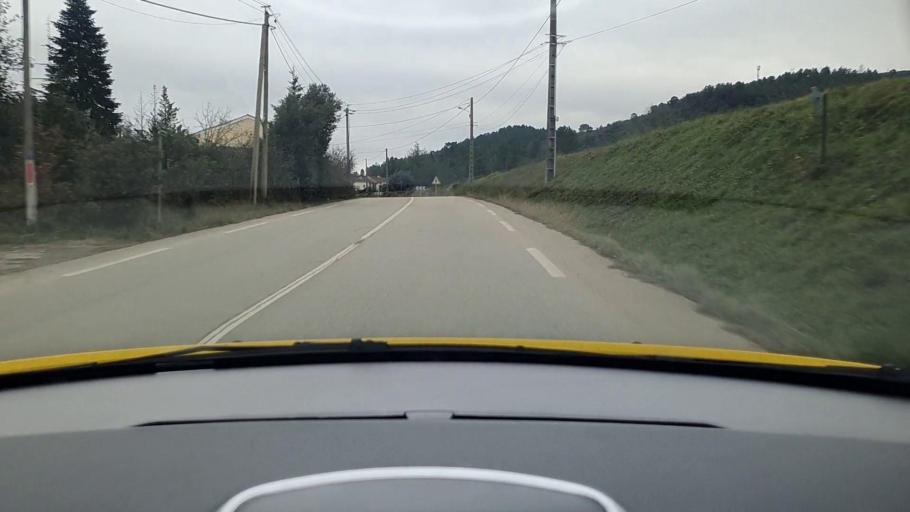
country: FR
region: Languedoc-Roussillon
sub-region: Departement du Gard
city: Laval-Pradel
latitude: 44.2260
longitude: 4.0641
